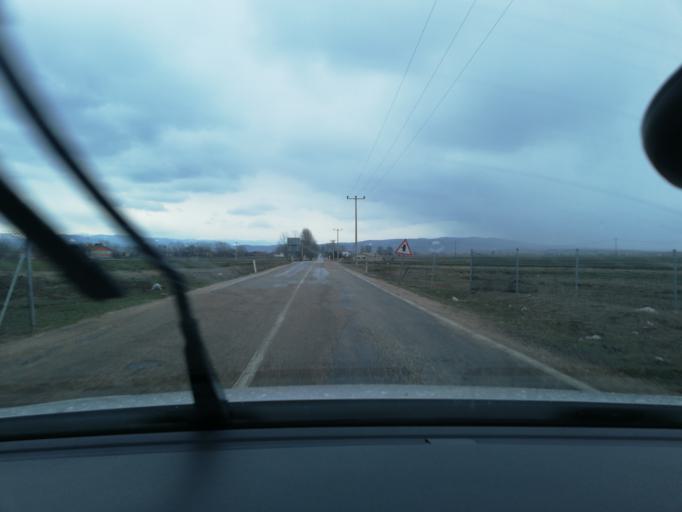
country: TR
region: Bolu
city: Dortdivan
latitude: 40.7410
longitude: 32.1153
